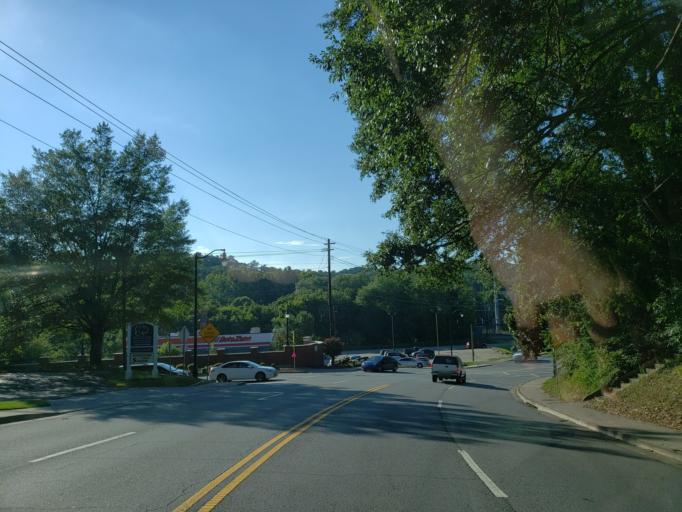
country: US
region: Georgia
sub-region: Cherokee County
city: Canton
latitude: 34.2378
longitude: -84.4944
